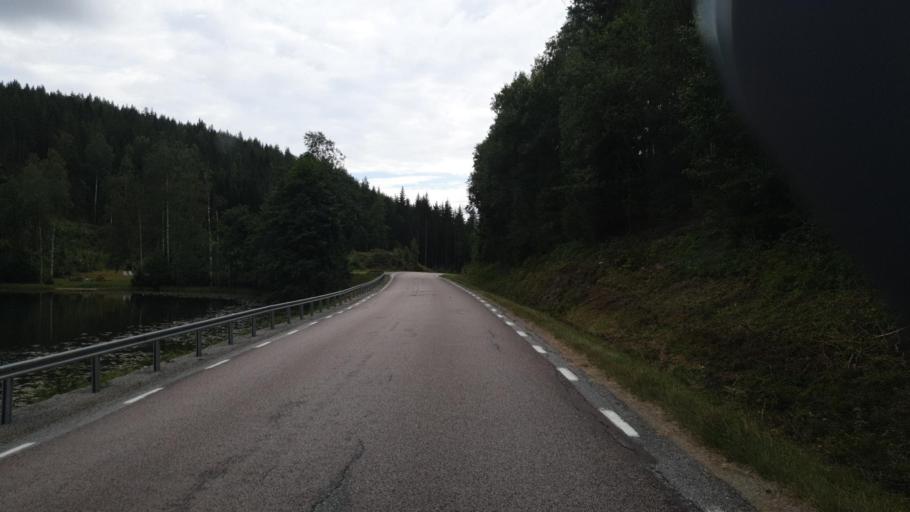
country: SE
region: Vaermland
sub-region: Arvika Kommun
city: Arvika
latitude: 59.6997
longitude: 12.7913
